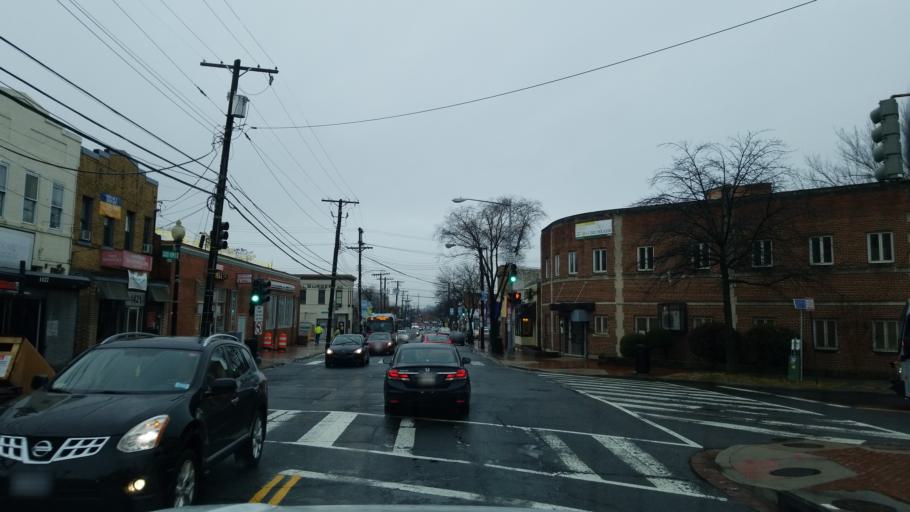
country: US
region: Maryland
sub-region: Prince George's County
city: Hillcrest Heights
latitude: 38.8666
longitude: -76.9841
